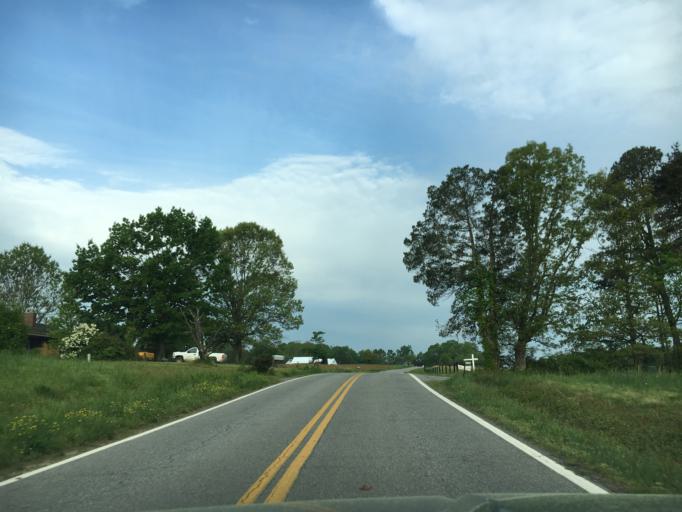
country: US
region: Virginia
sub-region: Halifax County
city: Halifax
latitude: 36.8935
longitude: -78.8465
